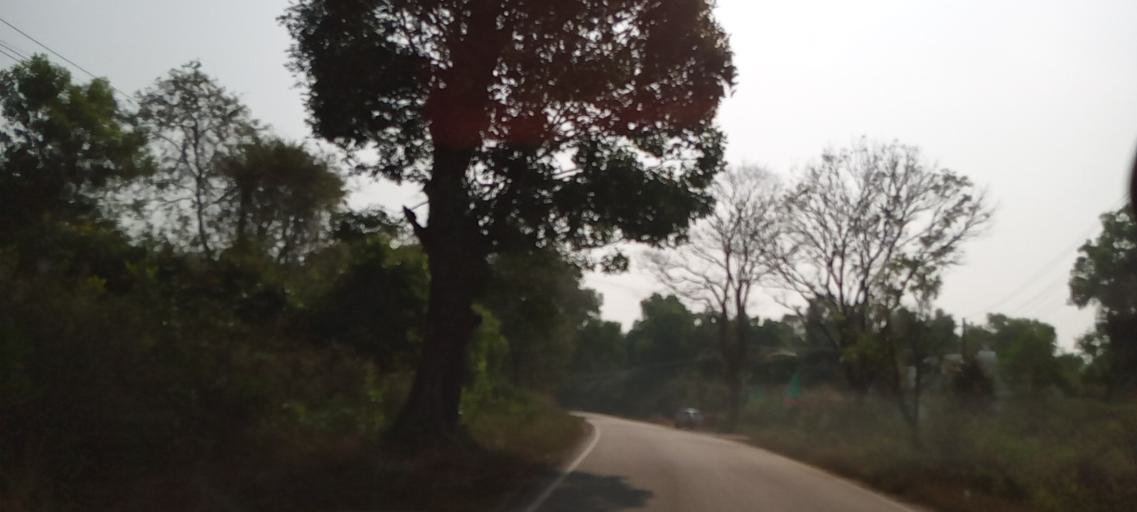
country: IN
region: Karnataka
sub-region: Udupi
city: Coondapoor
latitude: 13.5137
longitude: 74.8003
